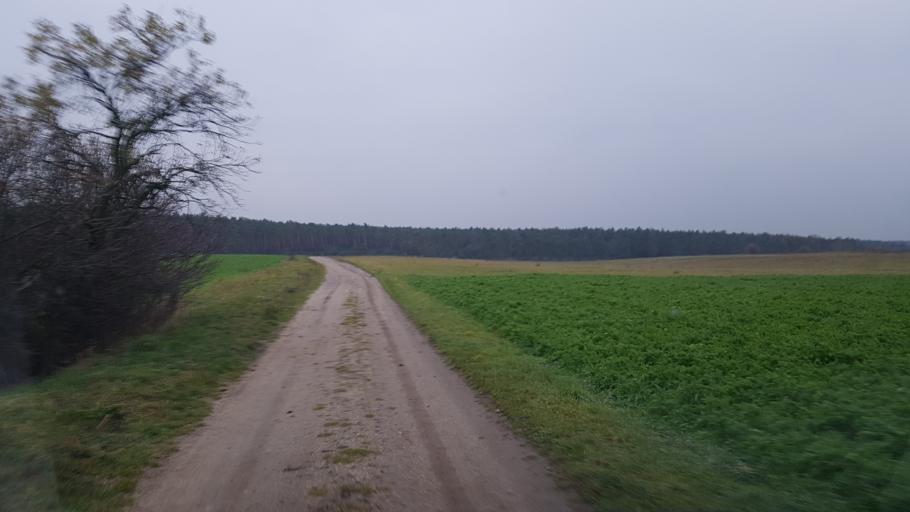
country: DE
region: Brandenburg
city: Trobitz
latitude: 51.6587
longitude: 13.4252
